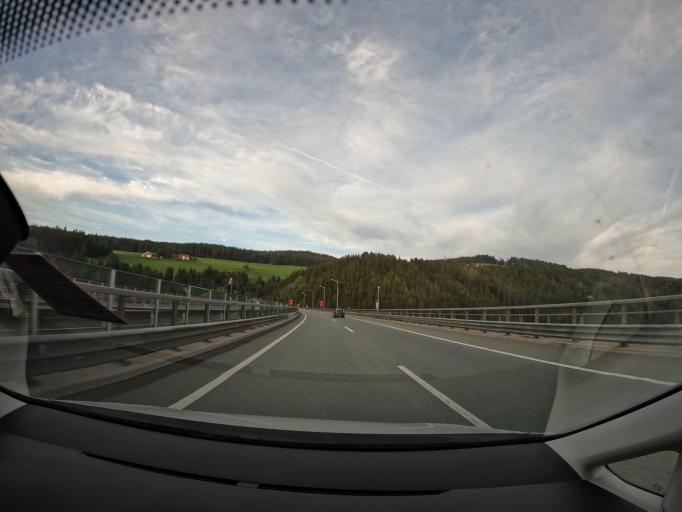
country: AT
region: Styria
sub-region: Politischer Bezirk Voitsberg
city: Pack
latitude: 46.9240
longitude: 14.9966
